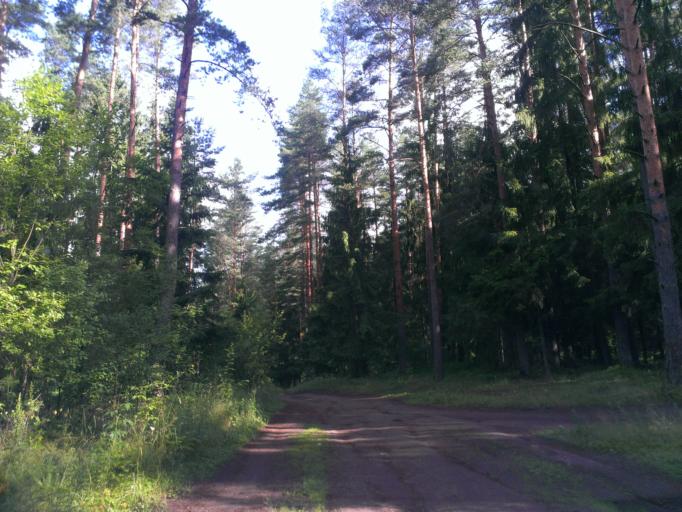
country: LV
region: Incukalns
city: Vangazi
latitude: 57.0978
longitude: 24.5416
